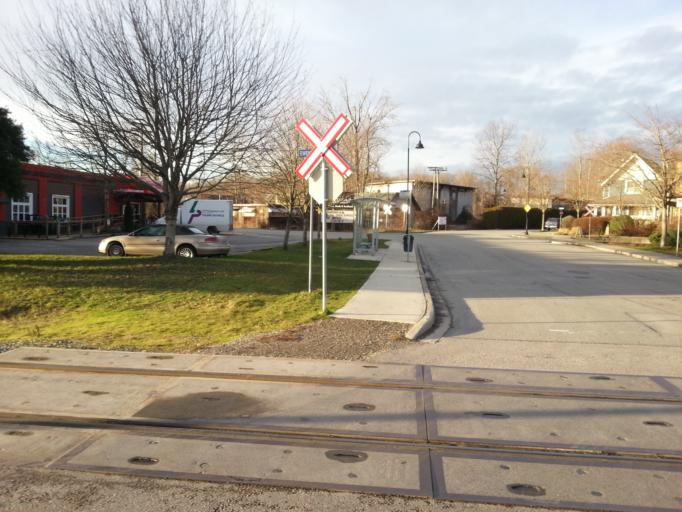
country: CA
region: British Columbia
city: New Westminster
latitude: 49.1945
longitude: -122.9271
